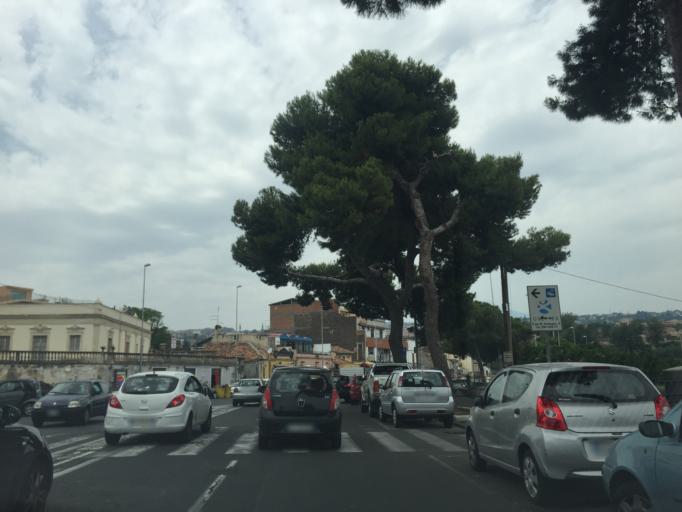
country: IT
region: Sicily
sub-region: Catania
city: Cerza
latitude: 37.5297
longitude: 15.1125
